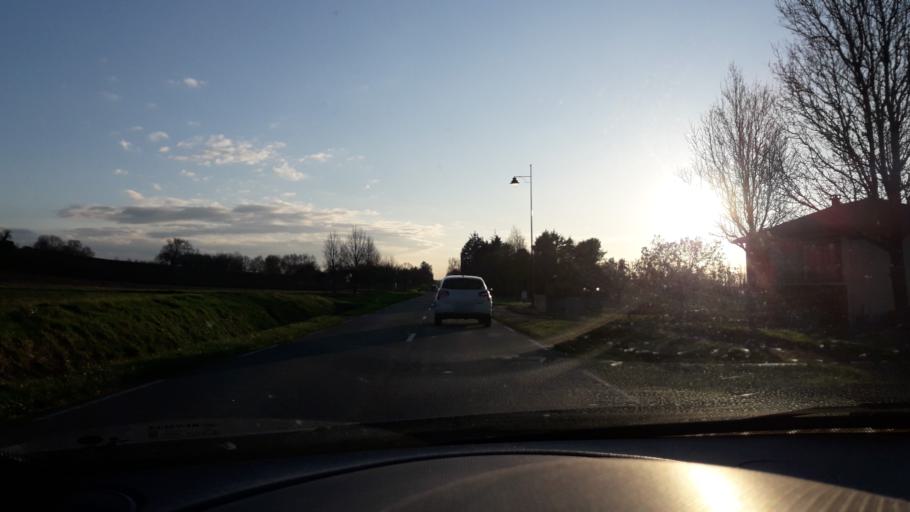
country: FR
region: Midi-Pyrenees
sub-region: Departement de la Haute-Garonne
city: Levignac
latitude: 43.6586
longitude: 1.1830
